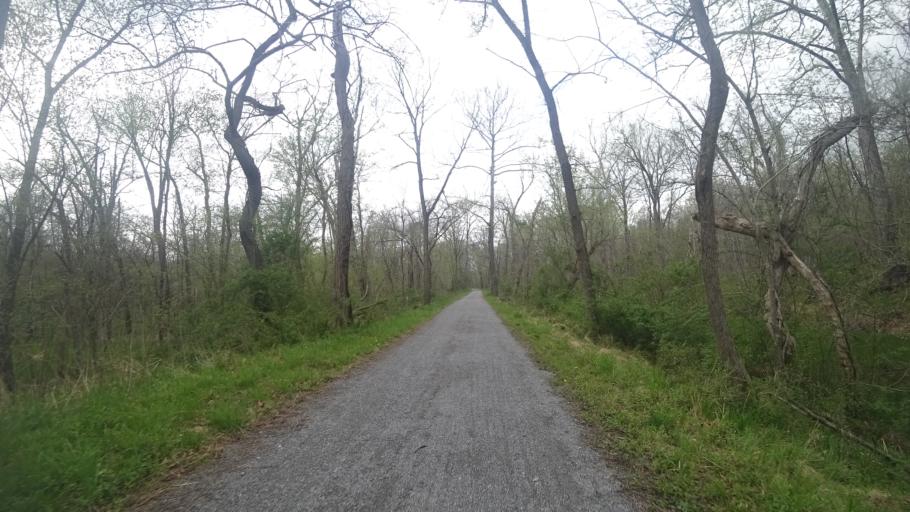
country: US
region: Virginia
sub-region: Loudoun County
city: Belmont
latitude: 39.1143
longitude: -77.4815
